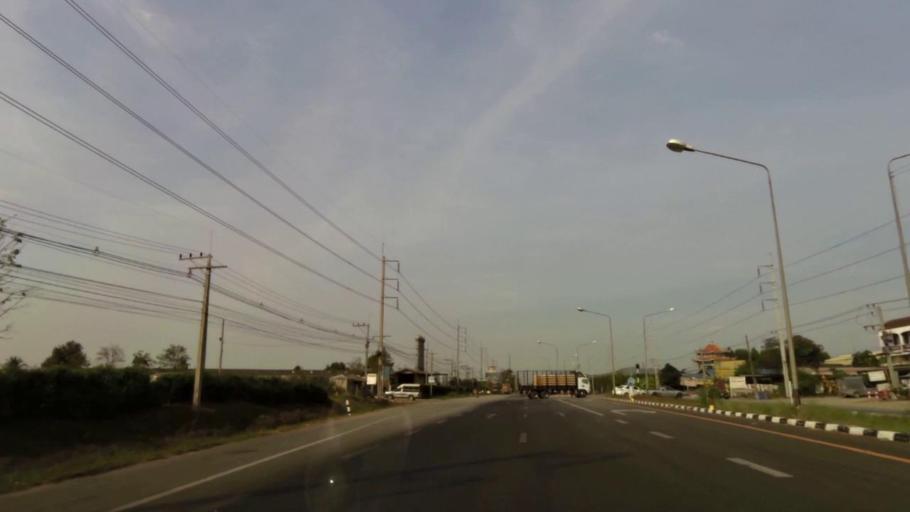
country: TH
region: Chon Buri
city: Nong Yai
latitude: 13.2003
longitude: 101.2445
